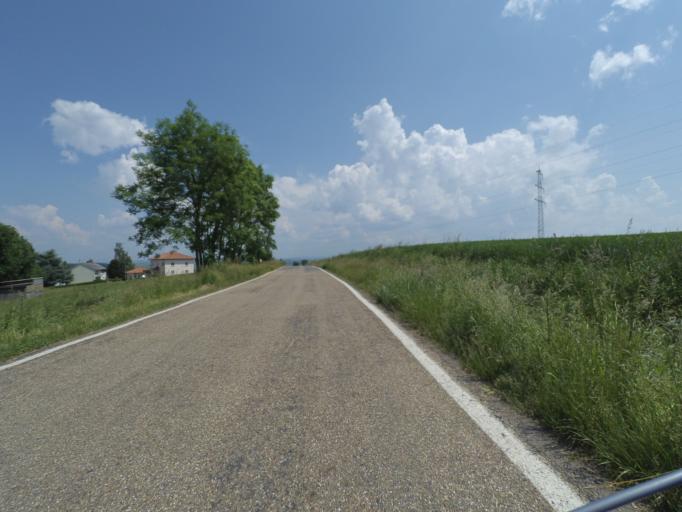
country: DE
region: Rheinland-Pfalz
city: Binningen
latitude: 50.2182
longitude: 7.2548
